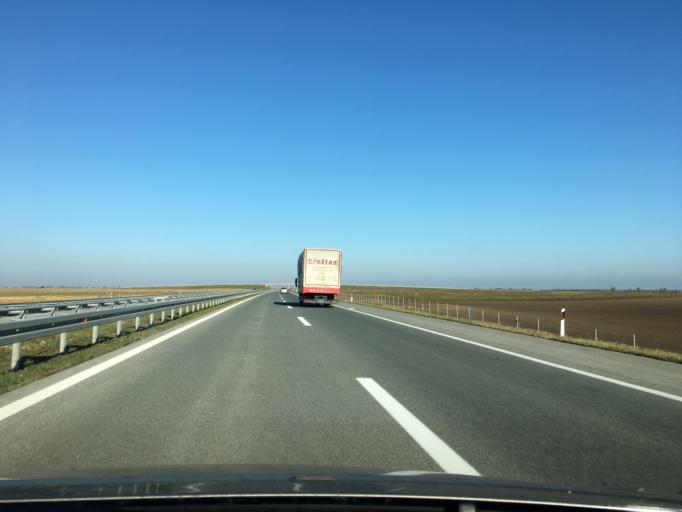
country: RS
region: Autonomna Pokrajina Vojvodina
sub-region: Severnobacki Okrug
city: Mali Igos
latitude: 45.7258
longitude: 19.7072
